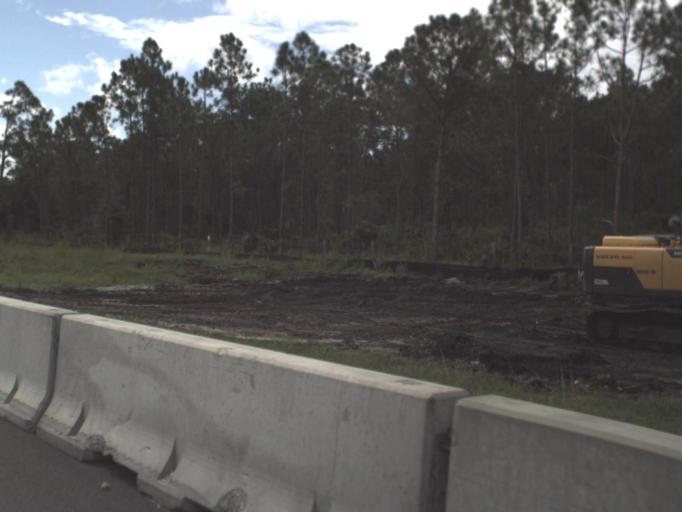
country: US
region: Florida
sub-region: Sarasota County
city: Warm Mineral Springs
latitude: 27.1097
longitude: -82.3120
